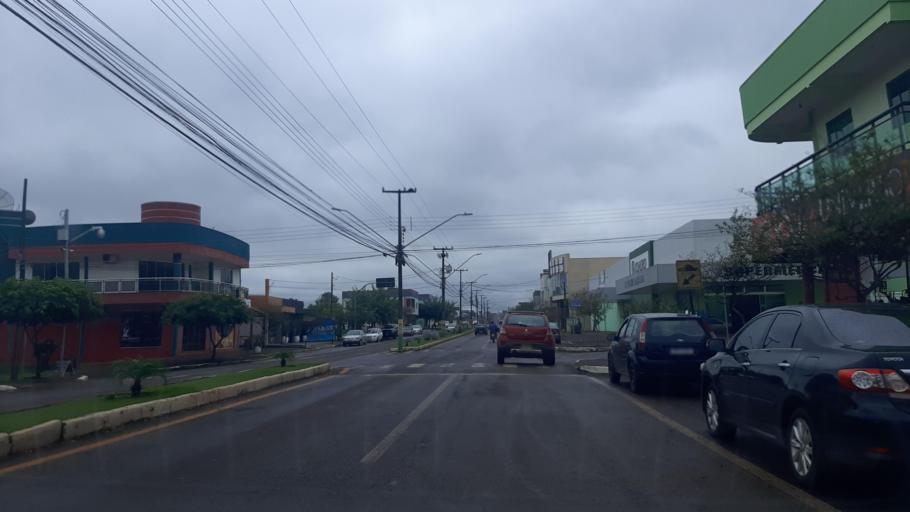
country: BR
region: Parana
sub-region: Santo Antonio Do Sudoeste
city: Santo Antonio do Sudoeste
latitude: -26.0617
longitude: -53.7261
